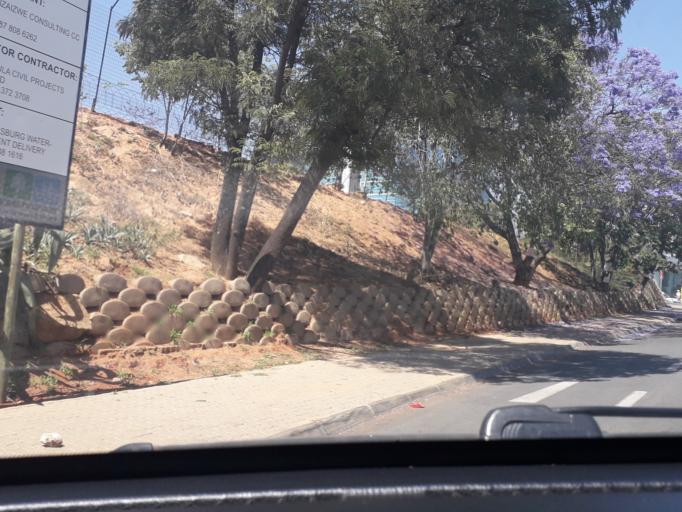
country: ZA
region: Gauteng
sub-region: City of Johannesburg Metropolitan Municipality
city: Johannesburg
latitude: -26.0959
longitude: 28.0576
